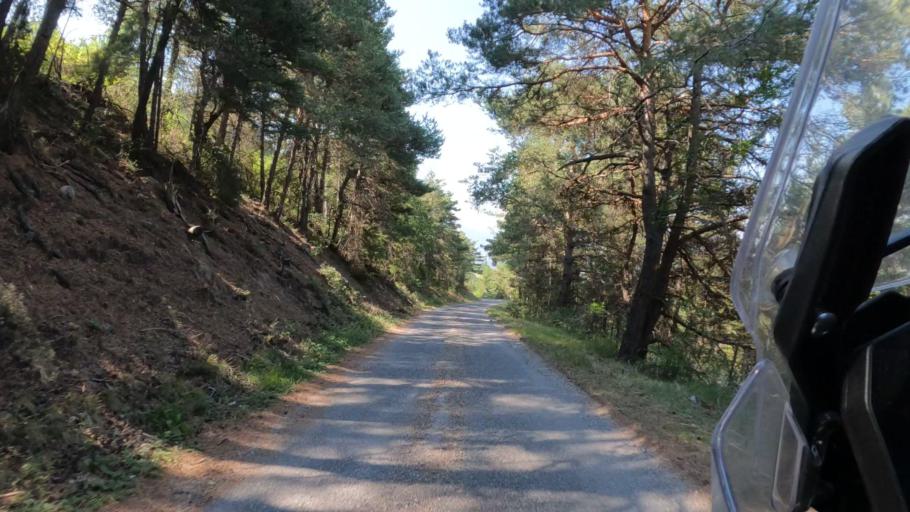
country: FR
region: Provence-Alpes-Cote d'Azur
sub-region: Departement des Hautes-Alpes
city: Embrun
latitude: 44.5942
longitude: 6.5451
